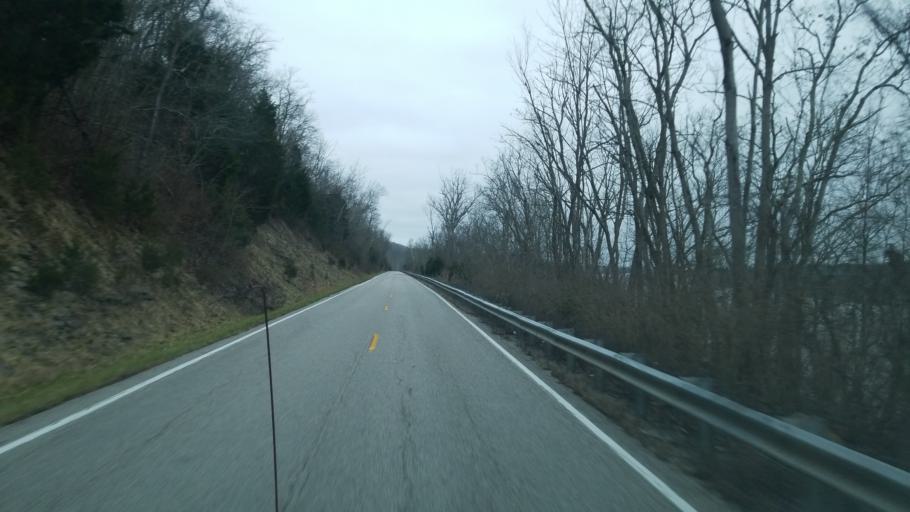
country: US
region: Kentucky
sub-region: Bracken County
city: Augusta
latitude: 38.7663
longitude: -84.0576
